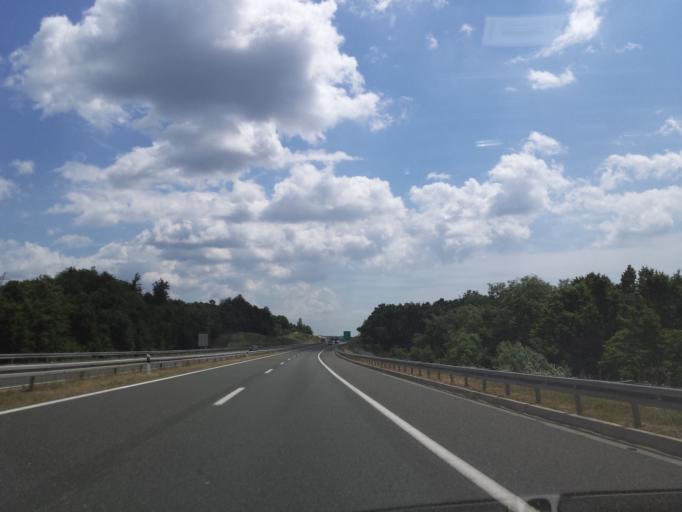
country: HR
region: Karlovacka
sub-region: Grad Ogulin
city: Ogulin
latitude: 45.4001
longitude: 15.2208
